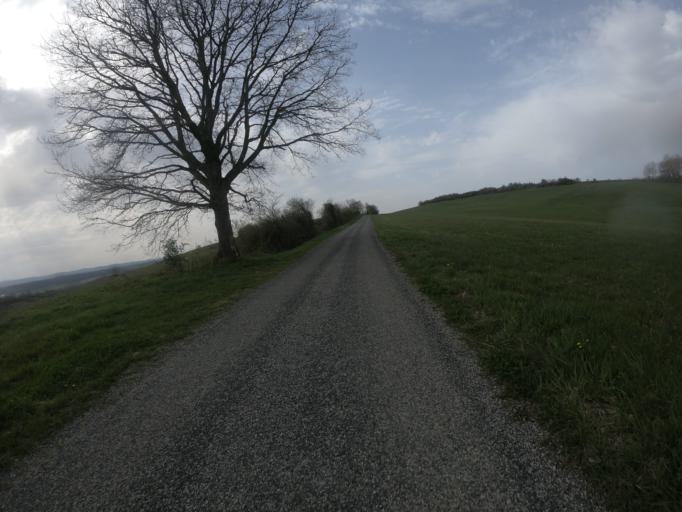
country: FR
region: Languedoc-Roussillon
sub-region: Departement de l'Aude
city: Belpech
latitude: 43.1299
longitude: 1.7605
